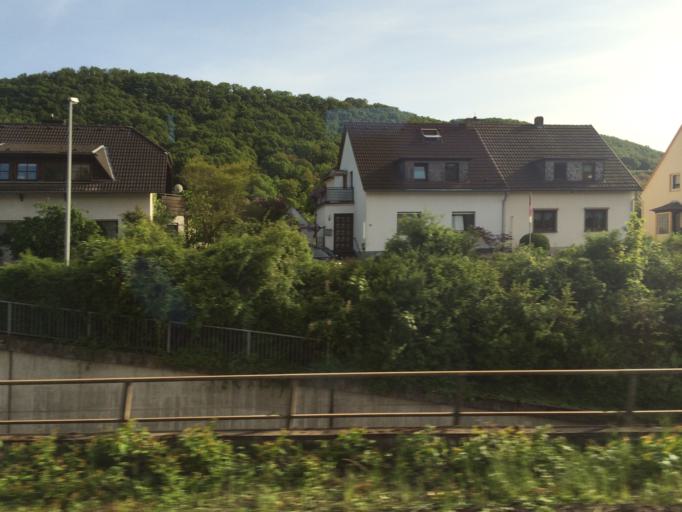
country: DE
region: Rheinland-Pfalz
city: Osterspai
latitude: 50.2464
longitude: 7.6098
